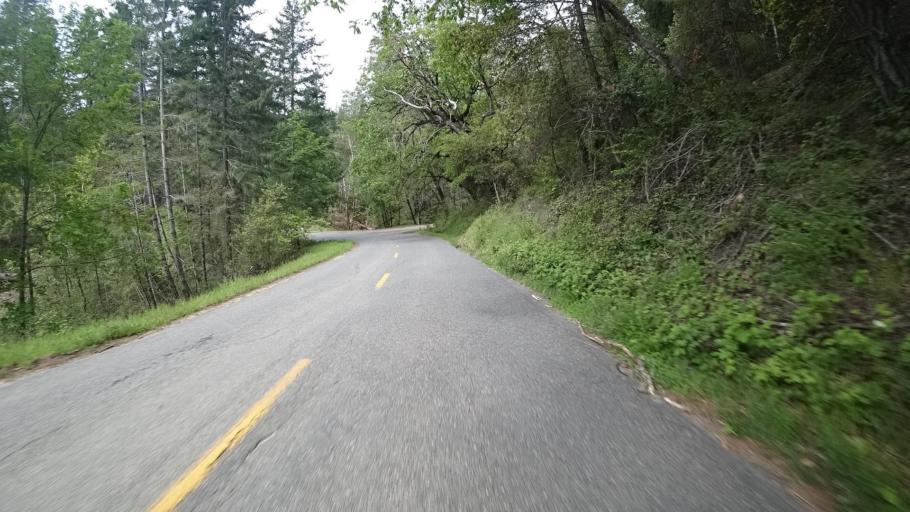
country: US
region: California
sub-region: Humboldt County
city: Redway
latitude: 40.1480
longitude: -123.6288
